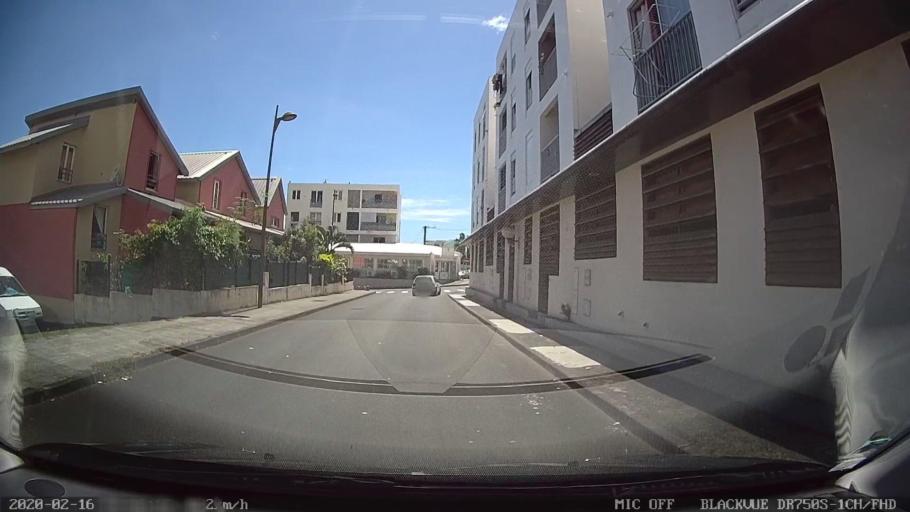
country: RE
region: Reunion
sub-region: Reunion
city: Saint-Denis
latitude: -20.8810
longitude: 55.4416
